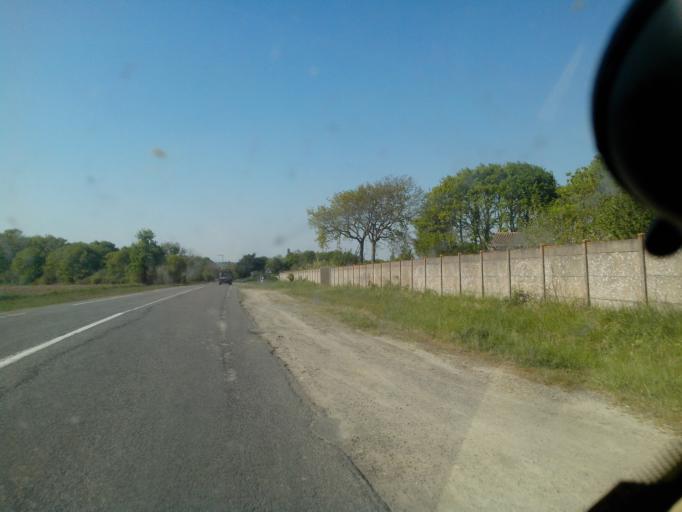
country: FR
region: Pays de la Loire
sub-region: Departement de la Loire-Atlantique
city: Pornic
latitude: 47.1070
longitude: -2.0736
